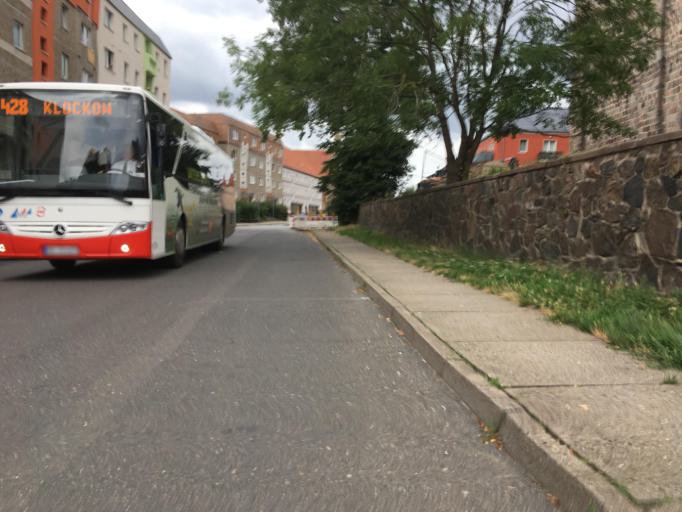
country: DE
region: Brandenburg
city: Prenzlau
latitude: 53.3133
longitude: 13.8558
